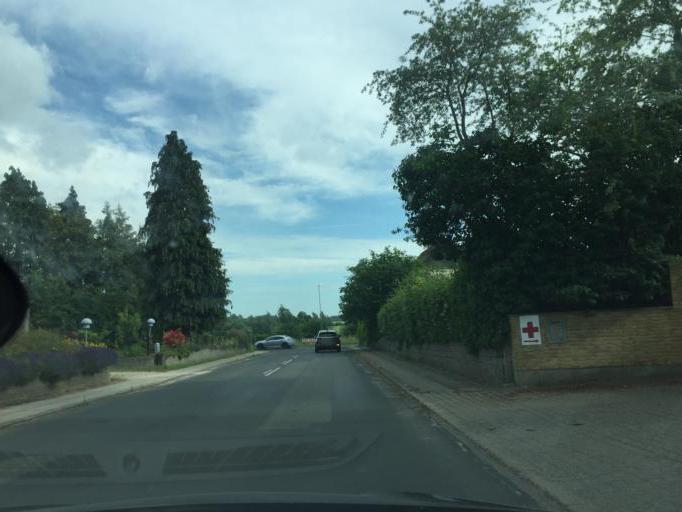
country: DK
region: South Denmark
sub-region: Faaborg-Midtfyn Kommune
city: Arslev
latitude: 55.3031
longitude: 10.4738
